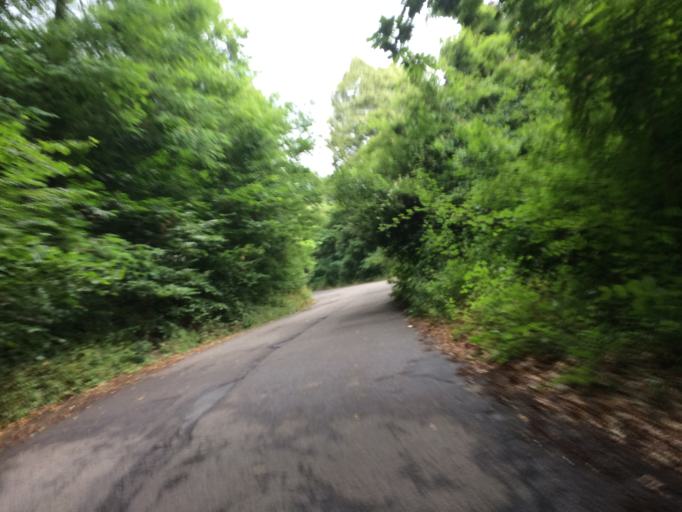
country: IT
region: Liguria
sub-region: Provincia di Imperia
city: Triora
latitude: 43.9852
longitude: 7.7657
